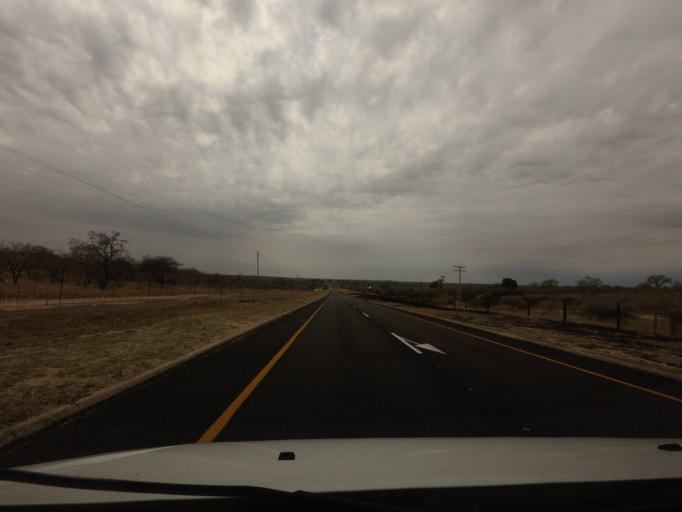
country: ZA
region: Limpopo
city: Thulamahashi
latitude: -24.5612
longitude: 31.1593
